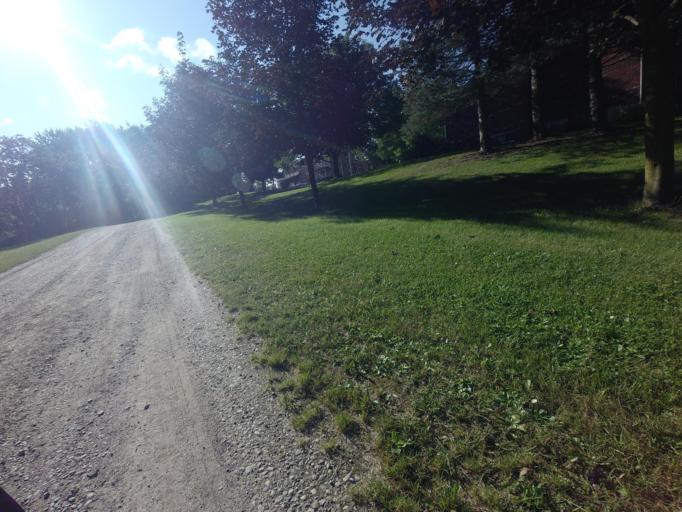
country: CA
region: Ontario
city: Huron East
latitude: 43.7384
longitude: -81.4305
